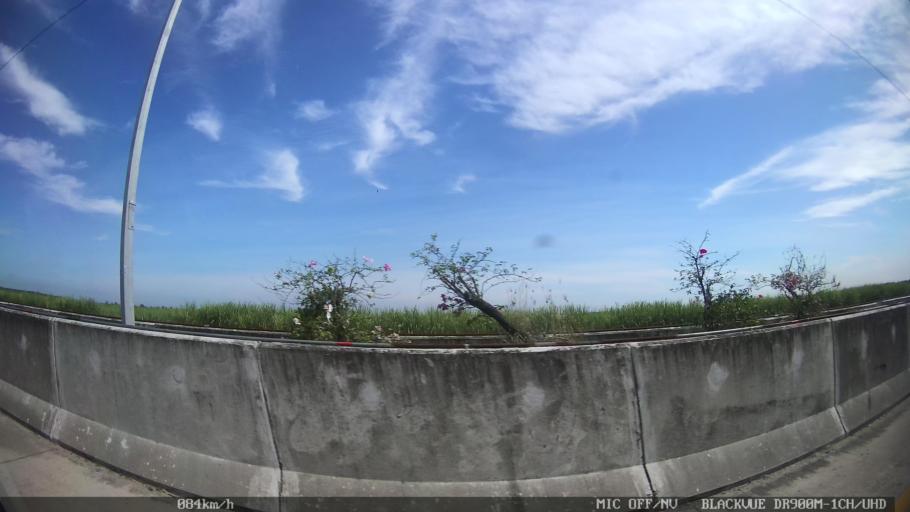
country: ID
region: North Sumatra
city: Sunggal
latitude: 3.6383
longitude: 98.6234
